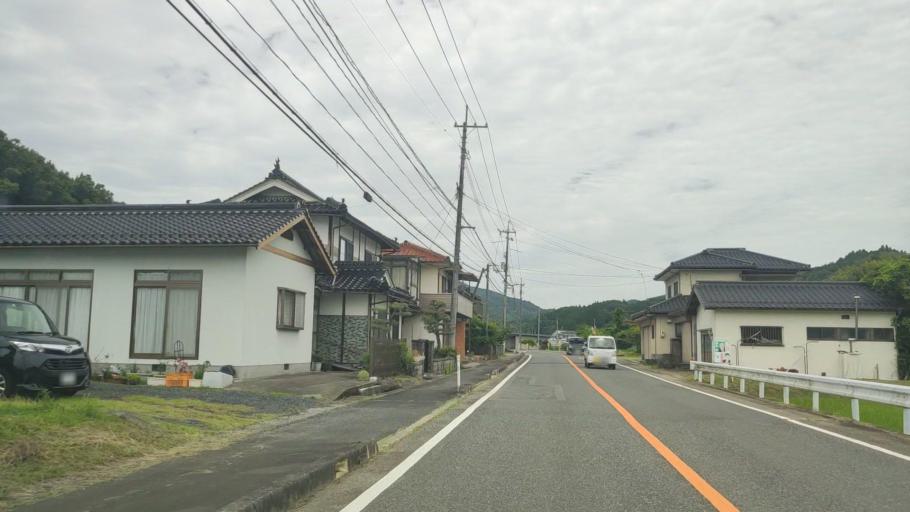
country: JP
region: Okayama
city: Tsuyama
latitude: 35.0715
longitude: 134.2408
